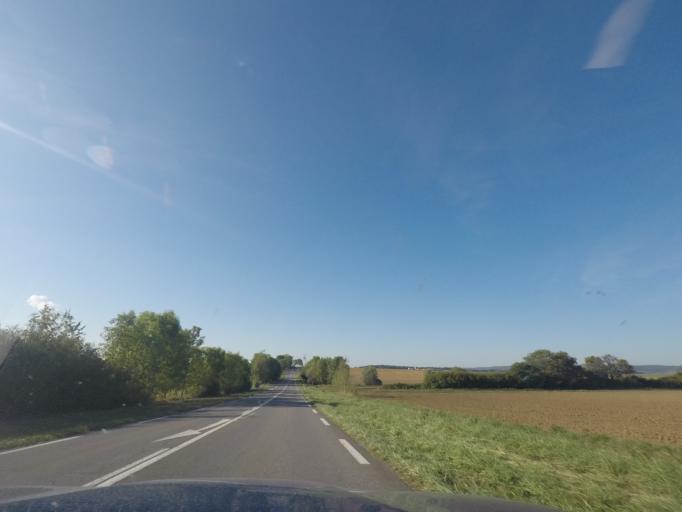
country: LU
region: Luxembourg
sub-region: Canton d'Esch-sur-Alzette
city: Frisange
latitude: 49.4680
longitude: 6.1843
